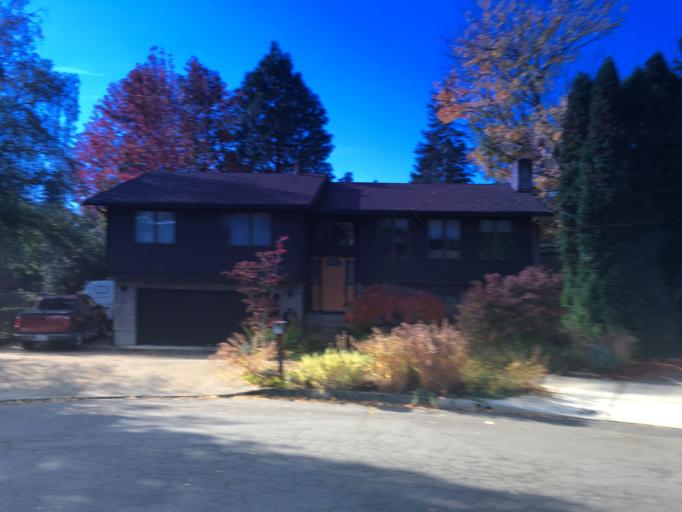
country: US
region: Oregon
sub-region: Multnomah County
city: Gresham
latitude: 45.5005
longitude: -122.3949
